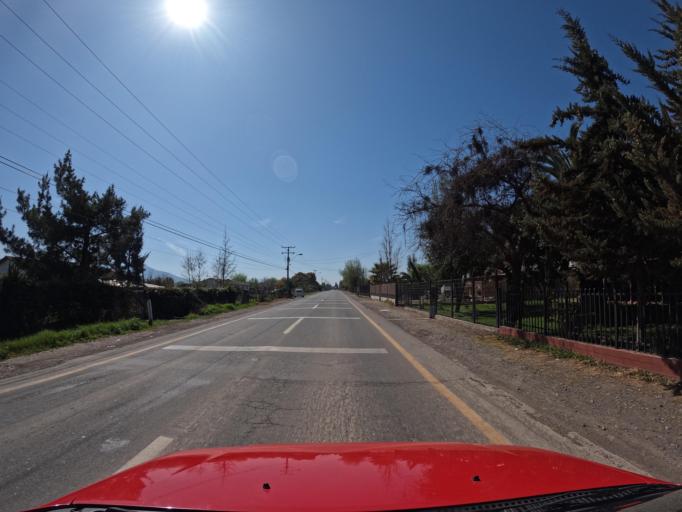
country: CL
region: Maule
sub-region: Provincia de Curico
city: Rauco
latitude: -35.0266
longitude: -71.4359
